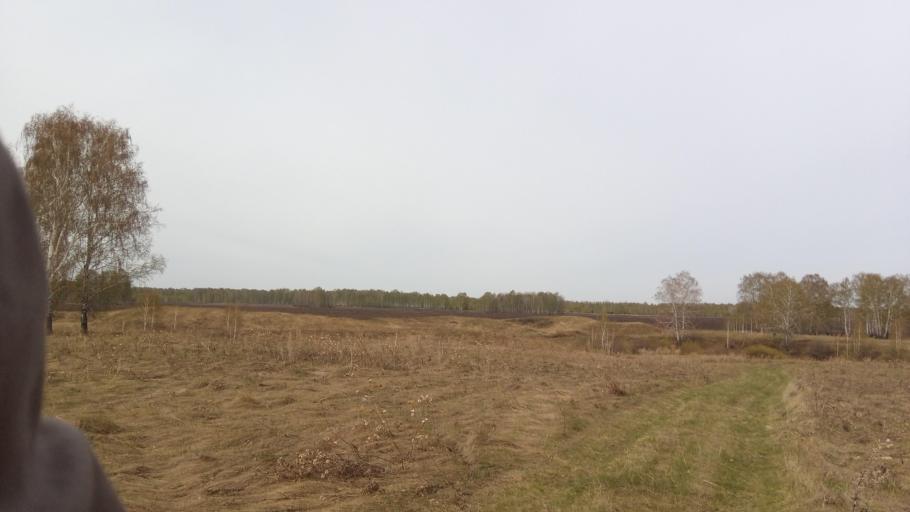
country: RU
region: Chelyabinsk
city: Timiryazevskiy
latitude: 55.0113
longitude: 60.8625
